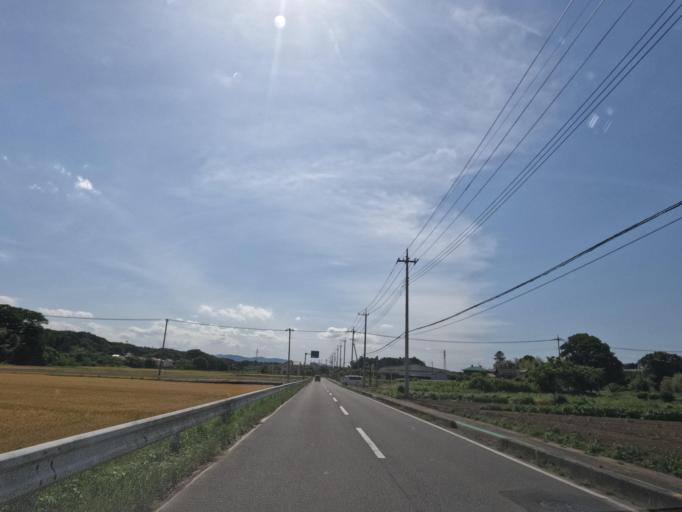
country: JP
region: Saitama
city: Kumagaya
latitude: 36.1052
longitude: 139.3382
